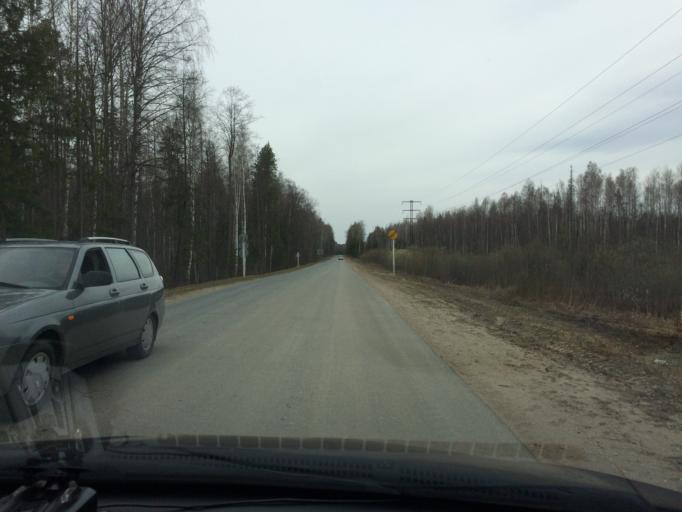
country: RU
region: Mariy-El
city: Surok
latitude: 56.5530
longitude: 48.3142
